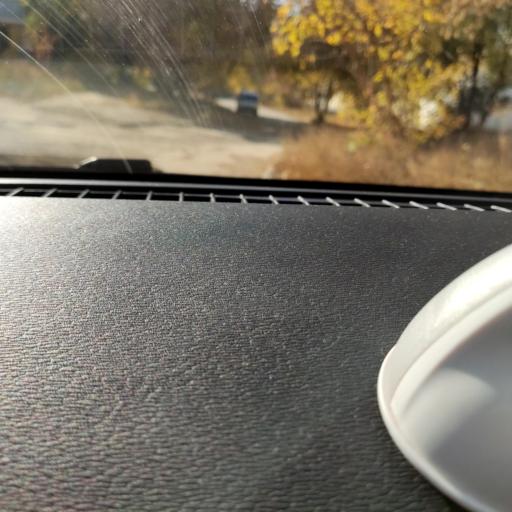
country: RU
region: Samara
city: Samara
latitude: 53.2008
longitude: 50.1454
